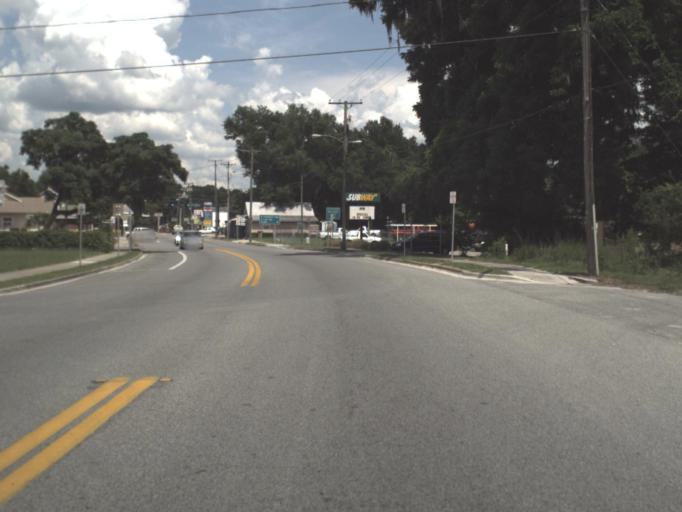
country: US
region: Florida
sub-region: Alachua County
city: High Springs
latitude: 29.9231
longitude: -82.7157
